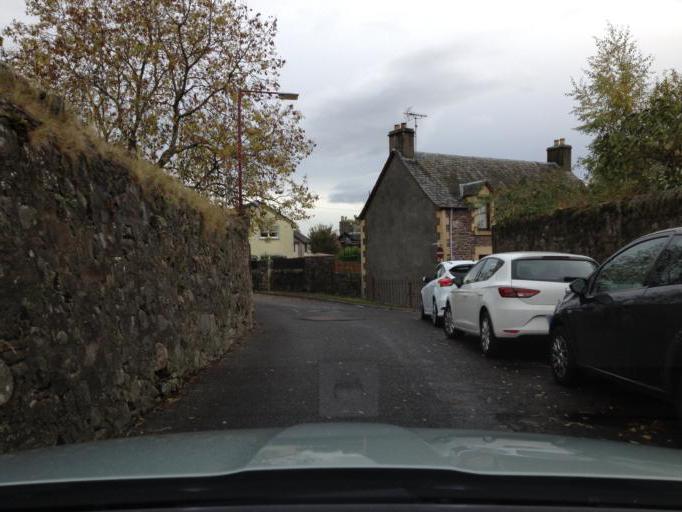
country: GB
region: Scotland
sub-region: Perth and Kinross
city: Crieff
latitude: 56.3720
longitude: -3.8384
